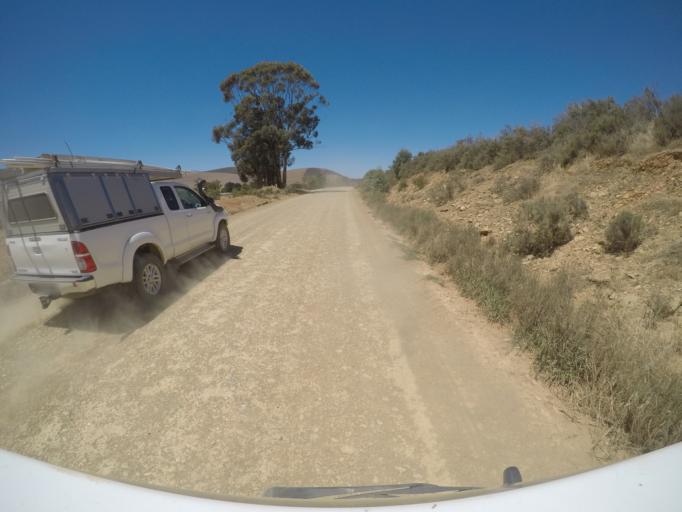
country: ZA
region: Western Cape
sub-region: Overberg District Municipality
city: Grabouw
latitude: -34.1010
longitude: 19.2050
